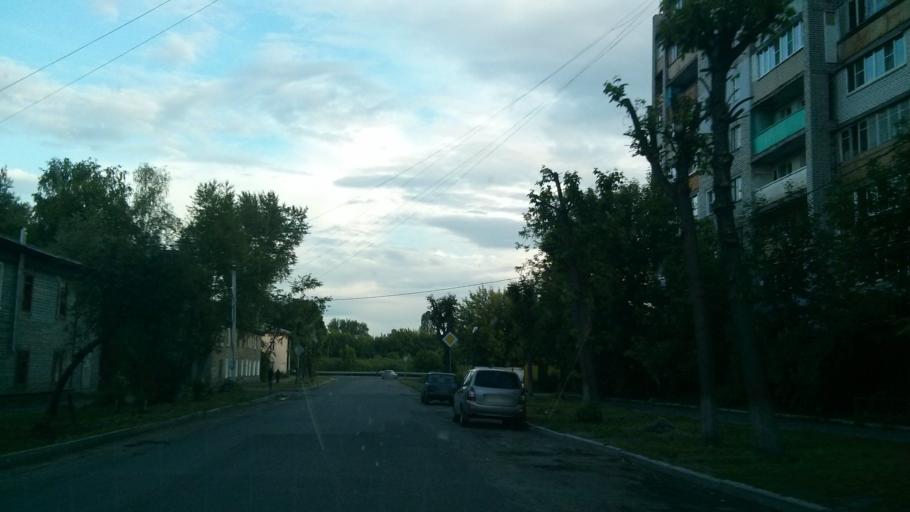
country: RU
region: Vladimir
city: Murom
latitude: 55.5667
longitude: 42.0519
